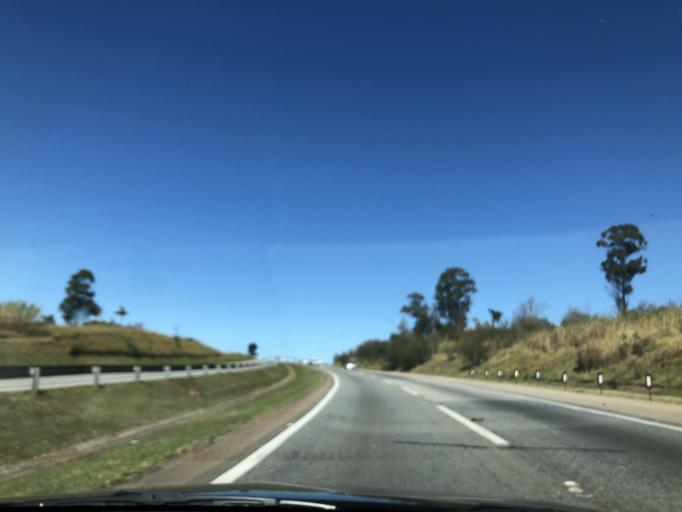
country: BR
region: Sao Paulo
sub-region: Sorocaba
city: Sorocaba
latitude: -23.4692
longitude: -47.3827
